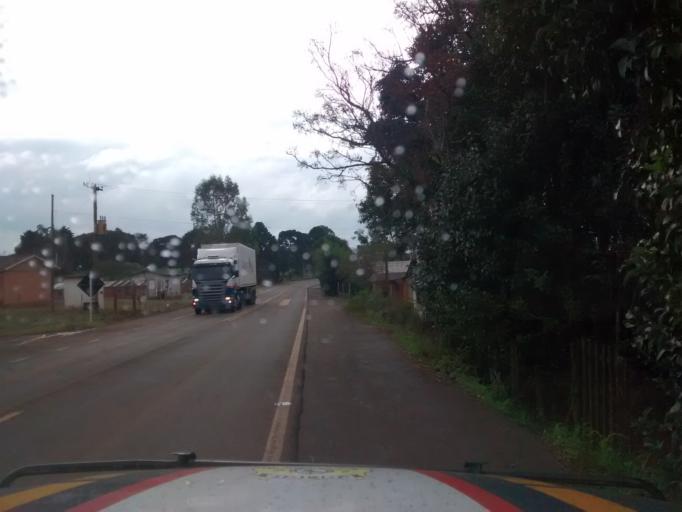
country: BR
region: Rio Grande do Sul
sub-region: Lagoa Vermelha
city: Lagoa Vermelha
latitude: -28.1946
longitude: -51.5252
